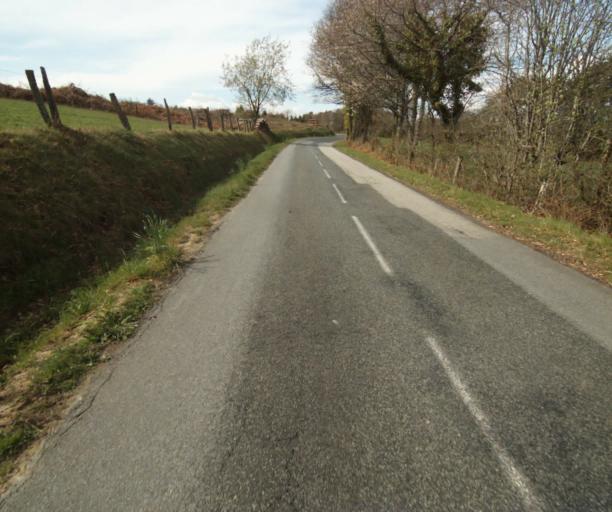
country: FR
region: Limousin
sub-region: Departement de la Correze
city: Correze
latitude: 45.3547
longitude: 1.9095
